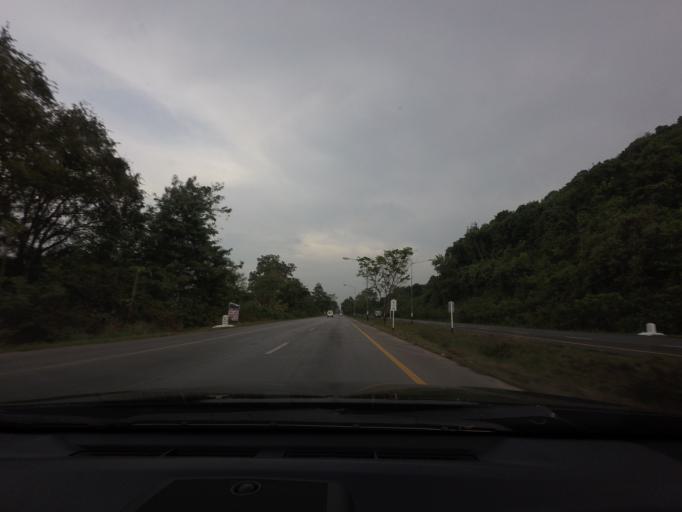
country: TH
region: Surat Thani
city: Tha Chana
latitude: 9.4904
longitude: 99.1376
